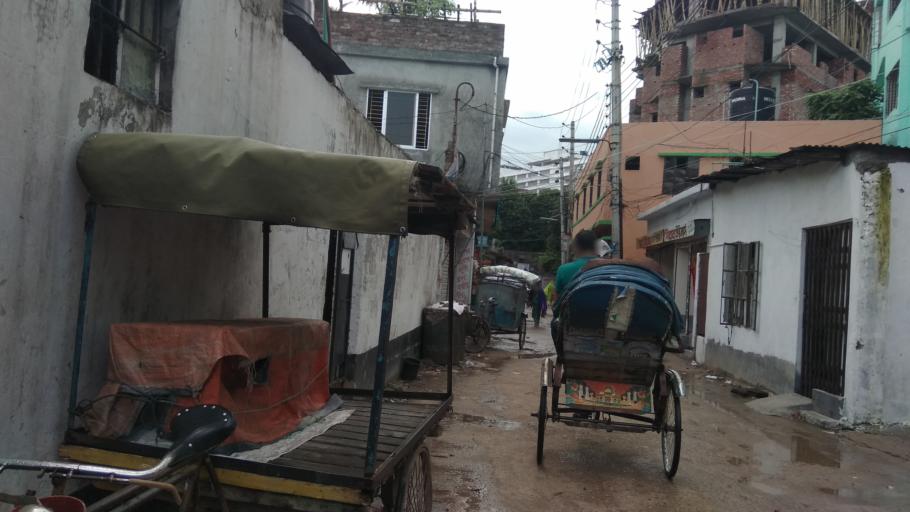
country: BD
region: Dhaka
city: Azimpur
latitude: 23.8006
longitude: 90.3781
